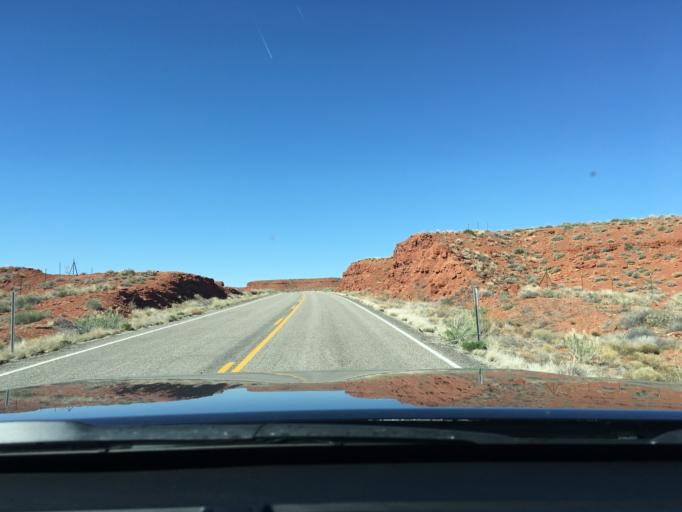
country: US
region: Utah
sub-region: San Juan County
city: Blanding
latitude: 37.2133
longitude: -109.8442
